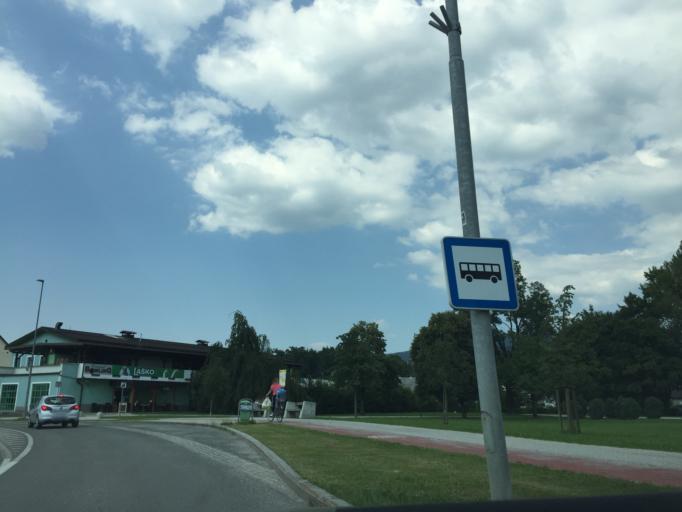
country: SI
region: Velenje
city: Velenje
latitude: 46.3685
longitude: 15.1042
